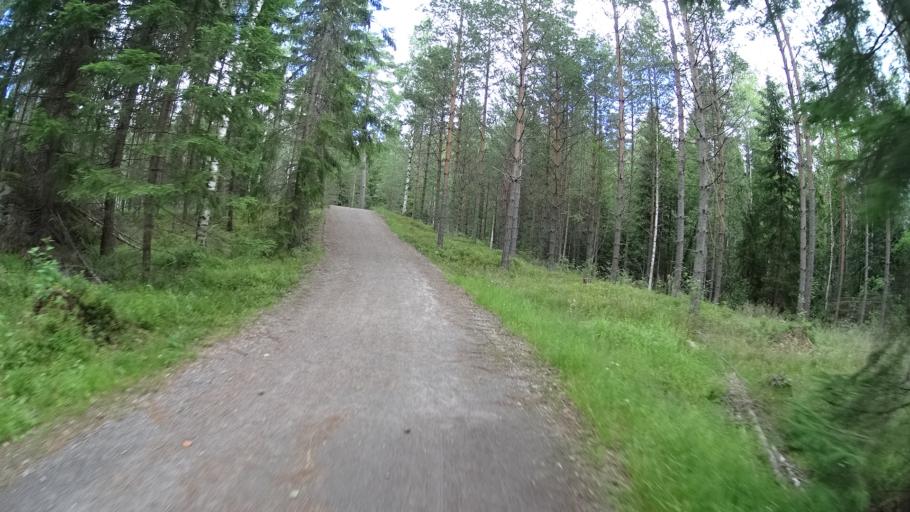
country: FI
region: Uusimaa
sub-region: Helsinki
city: Espoo
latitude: 60.2704
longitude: 24.6185
